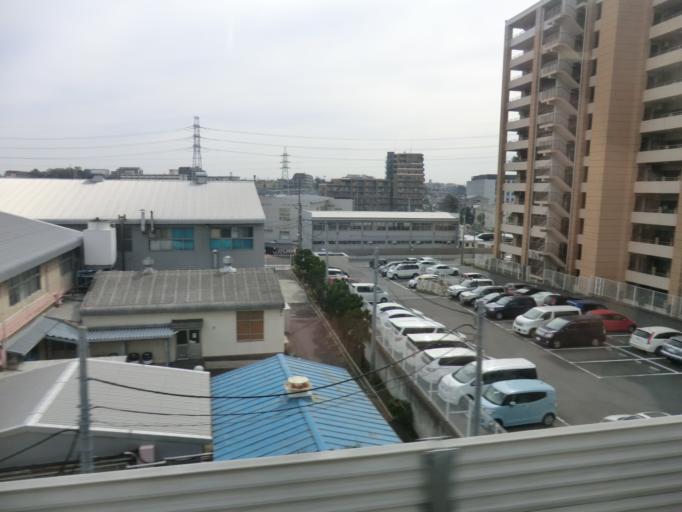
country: JP
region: Chiba
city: Funabashi
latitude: 35.7150
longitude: 139.9804
